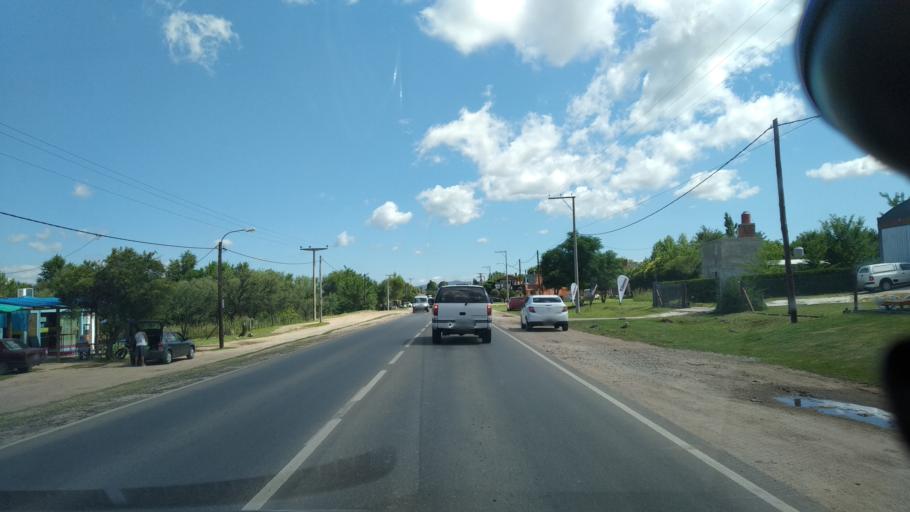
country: AR
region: Cordoba
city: Mina Clavero
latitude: -31.7708
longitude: -65.0007
